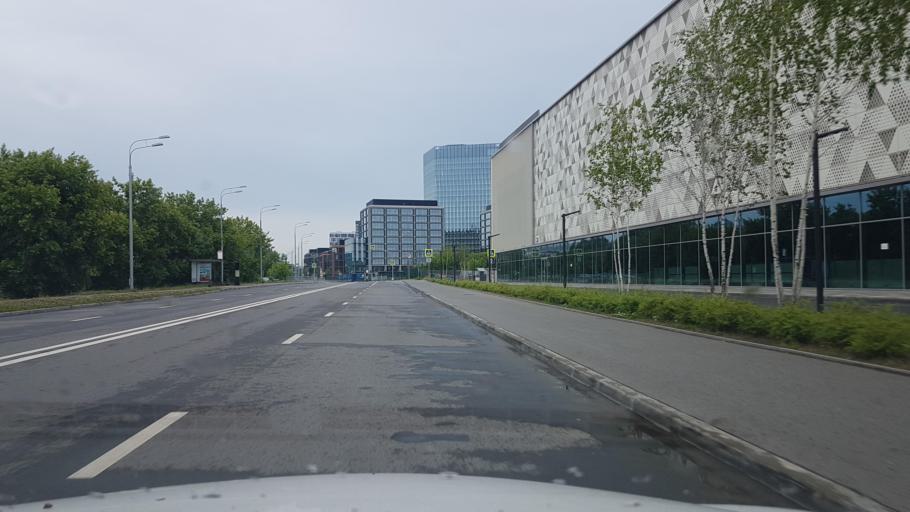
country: RU
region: Moscow
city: Strogino
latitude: 55.8237
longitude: 37.4184
